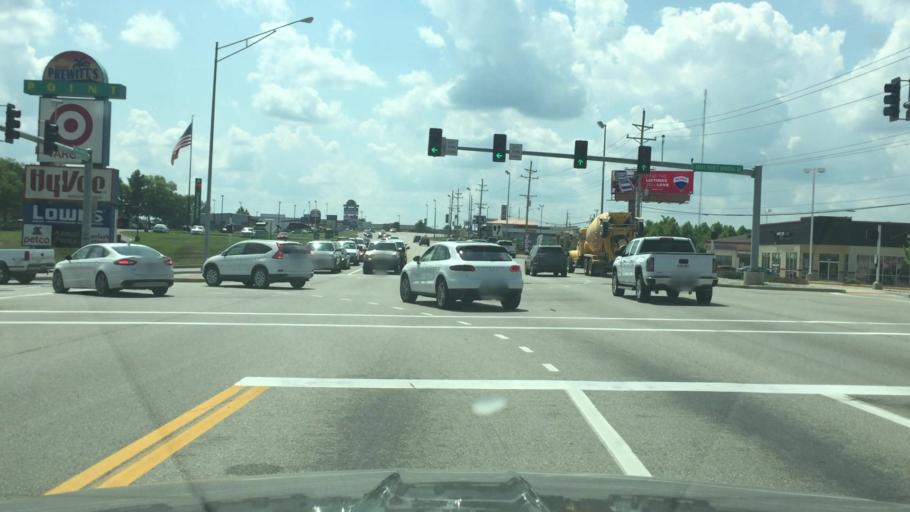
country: US
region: Missouri
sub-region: Miller County
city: Lake Ozark
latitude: 38.1619
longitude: -92.6078
